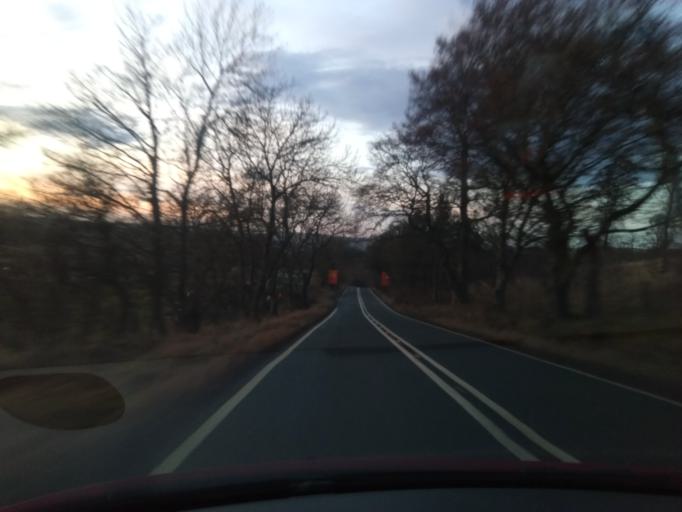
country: GB
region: England
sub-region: Northumberland
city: Otterburn
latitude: 55.2295
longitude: -2.1695
